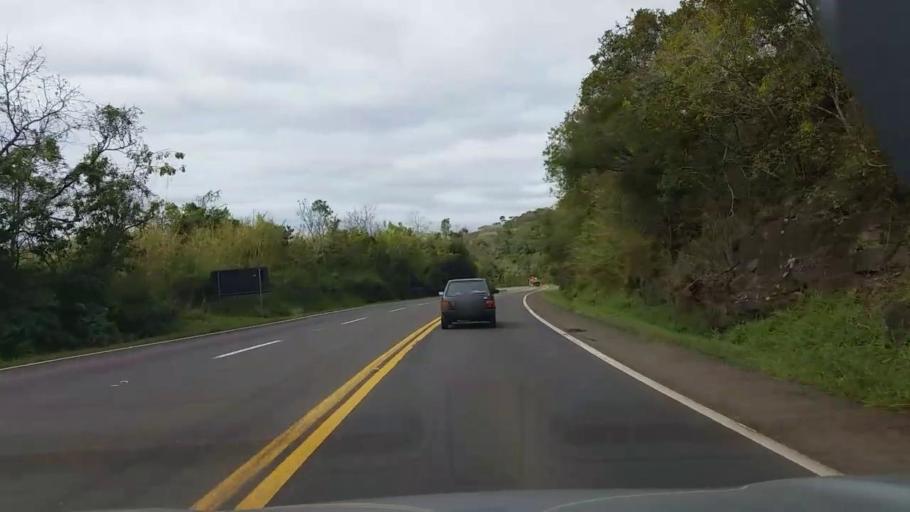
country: BR
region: Rio Grande do Sul
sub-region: Arroio Do Meio
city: Arroio do Meio
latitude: -29.3863
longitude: -52.0506
